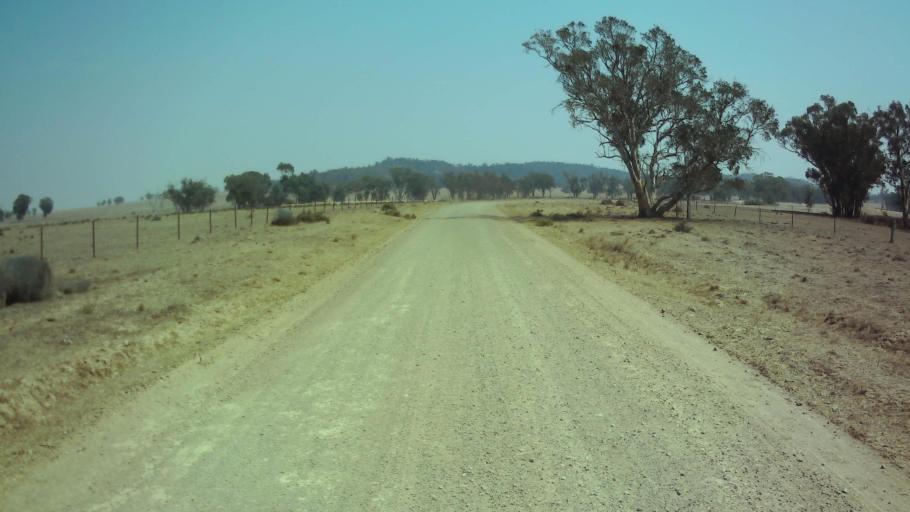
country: AU
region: New South Wales
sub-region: Weddin
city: Grenfell
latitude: -33.6770
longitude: 148.2762
